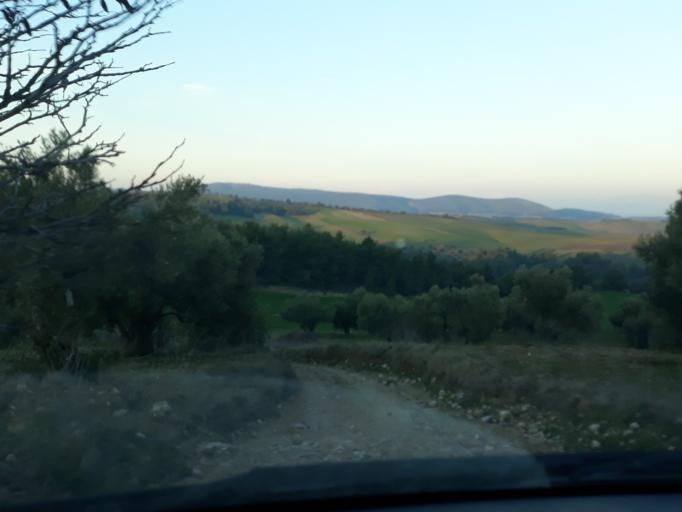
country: GR
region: Central Greece
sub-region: Nomos Voiotias
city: Asopia
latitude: 38.2791
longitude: 23.5303
